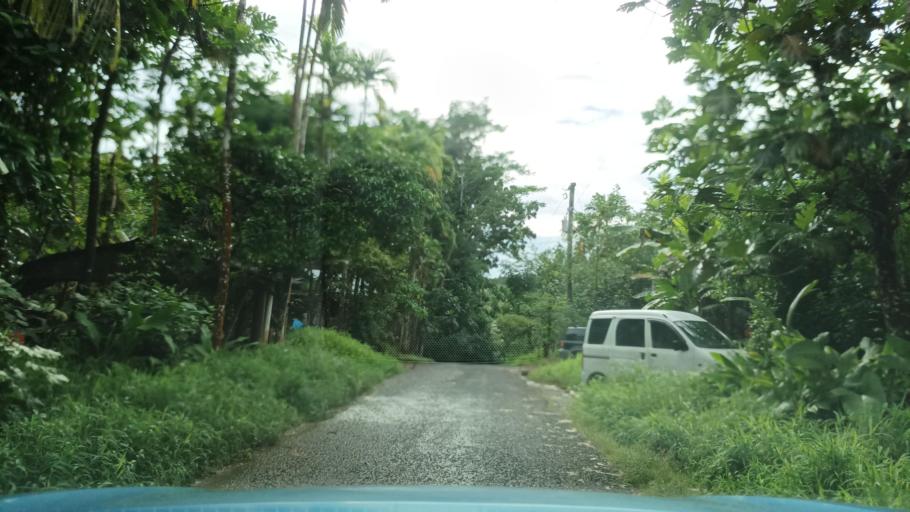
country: FM
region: Pohnpei
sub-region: Sokehs Municipality
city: Palikir - National Government Center
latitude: 6.8769
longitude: 158.1625
